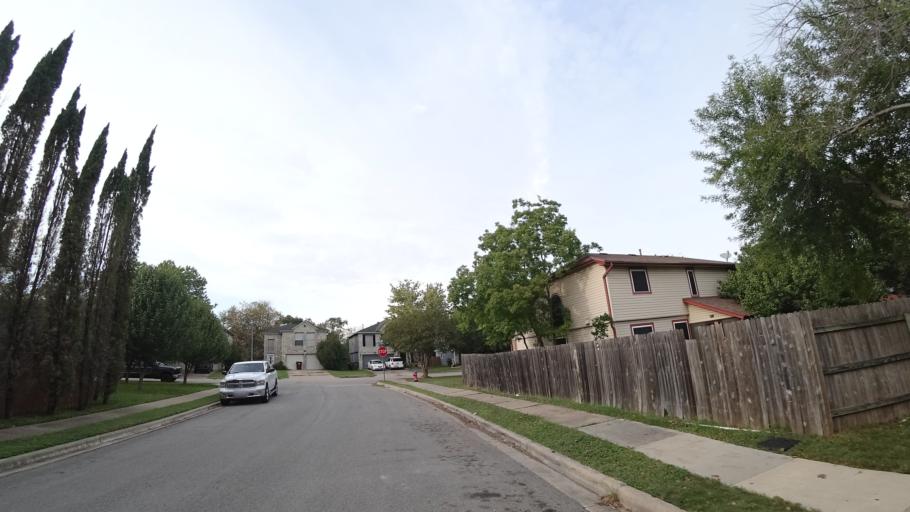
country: US
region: Texas
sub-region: Williamson County
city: Round Rock
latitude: 30.5063
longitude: -97.6625
